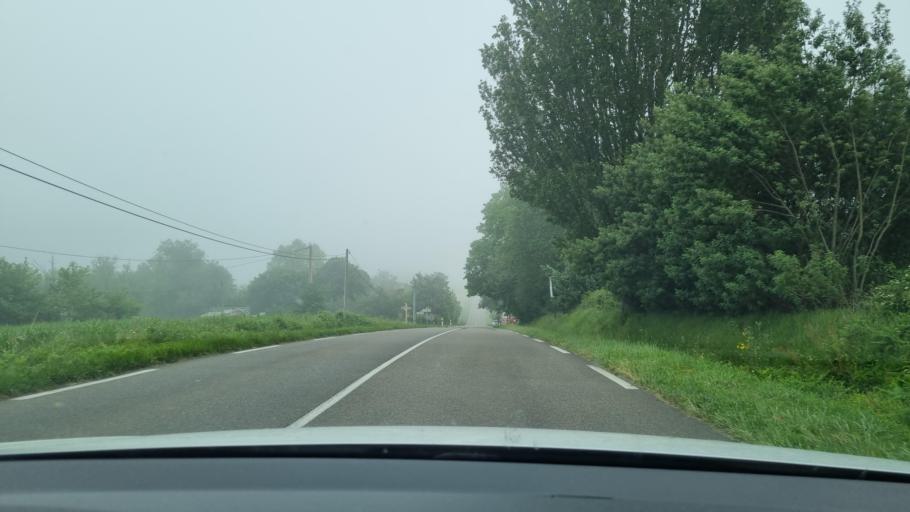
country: FR
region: Aquitaine
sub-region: Departement des Landes
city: Amou
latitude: 43.5768
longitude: -0.6574
